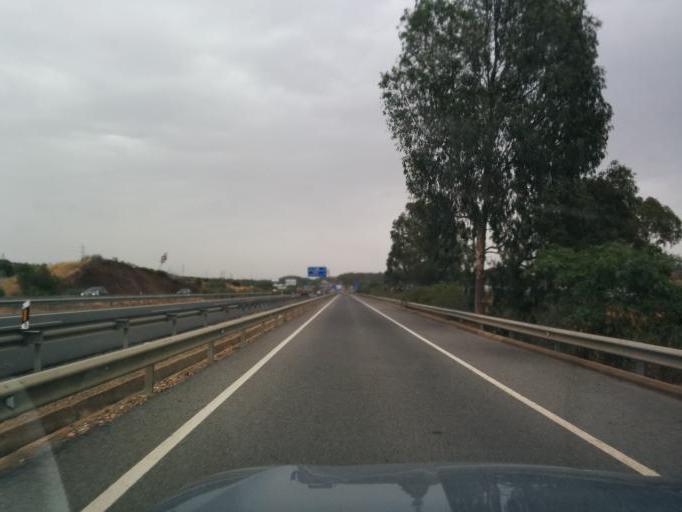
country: ES
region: Andalusia
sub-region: Provincia de Huelva
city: Ayamonte
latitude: 37.2386
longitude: -7.3908
